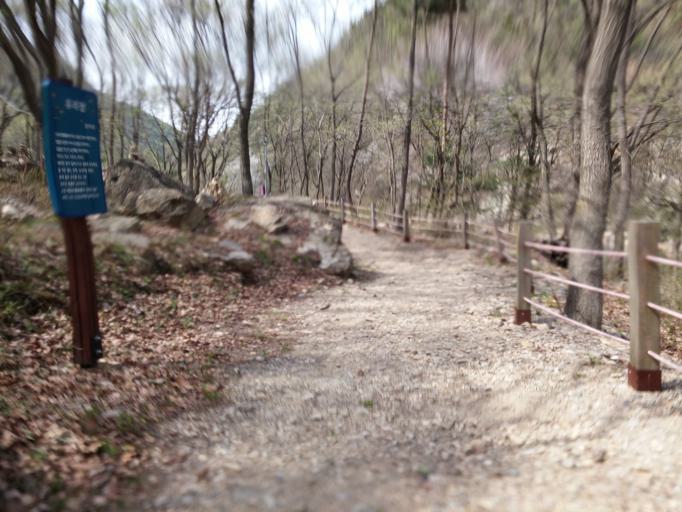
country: KR
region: Chungcheongbuk-do
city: Okcheon
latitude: 36.2357
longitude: 127.5601
